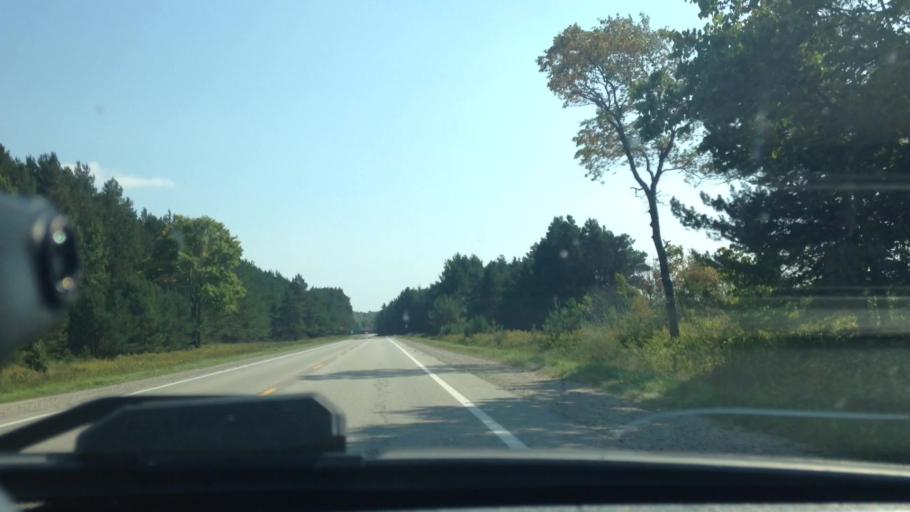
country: US
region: Michigan
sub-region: Luce County
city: Newberry
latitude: 46.3172
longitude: -85.6648
